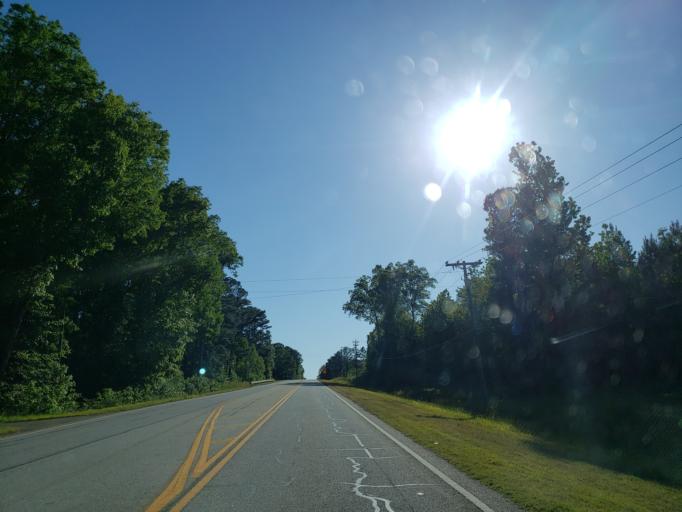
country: US
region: Georgia
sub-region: Haralson County
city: Buchanan
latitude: 33.8067
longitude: -85.1606
